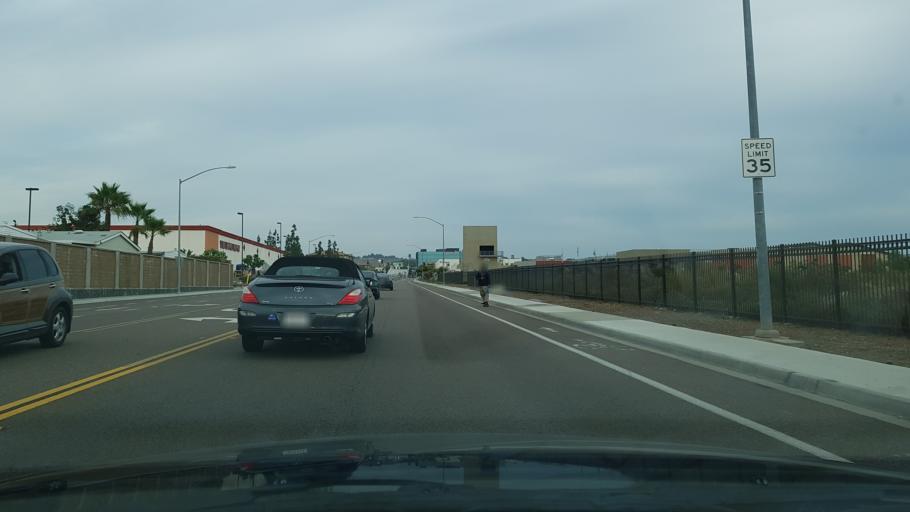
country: US
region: California
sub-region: San Diego County
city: Poway
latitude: 32.9129
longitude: -117.1236
